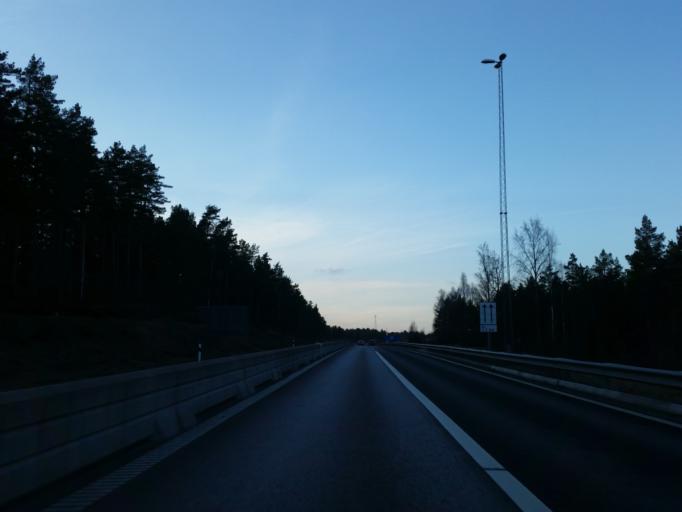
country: SE
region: Kalmar
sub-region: Oskarshamns Kommun
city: Oskarshamn
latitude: 57.3756
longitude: 16.4871
